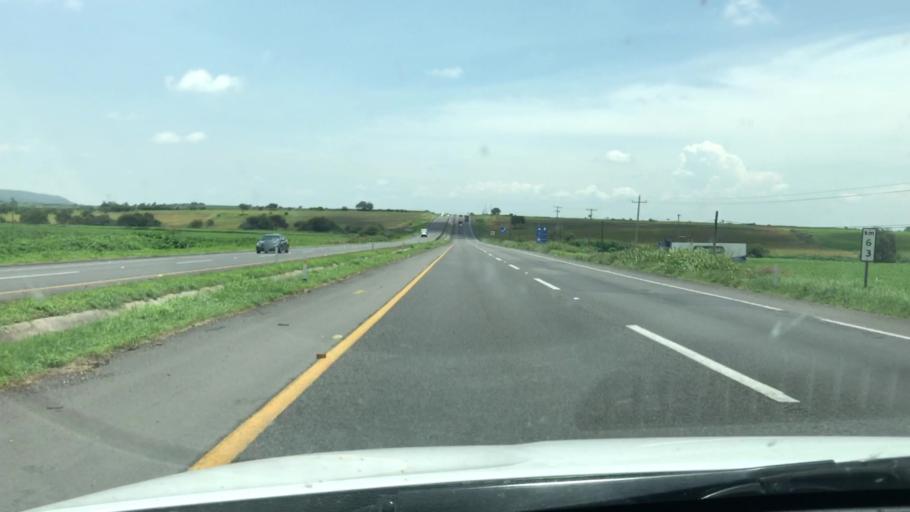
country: MX
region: Guanajuato
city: Penjamo
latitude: 20.3813
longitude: -101.8177
